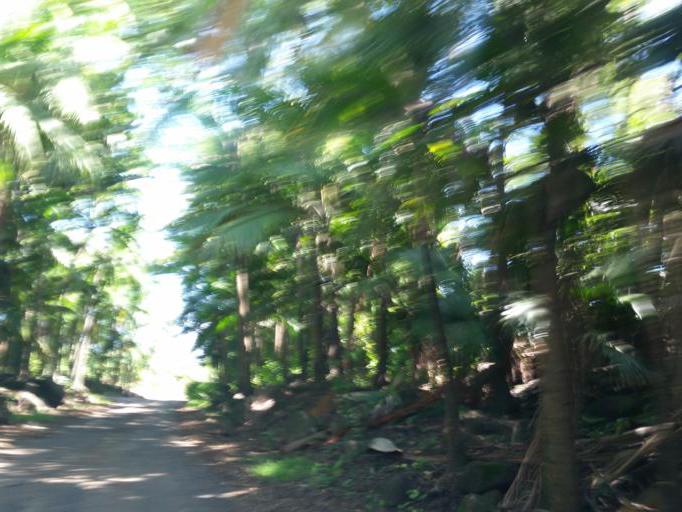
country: RE
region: Reunion
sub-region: Reunion
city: Sainte-Marie
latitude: -20.9064
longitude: 55.5152
